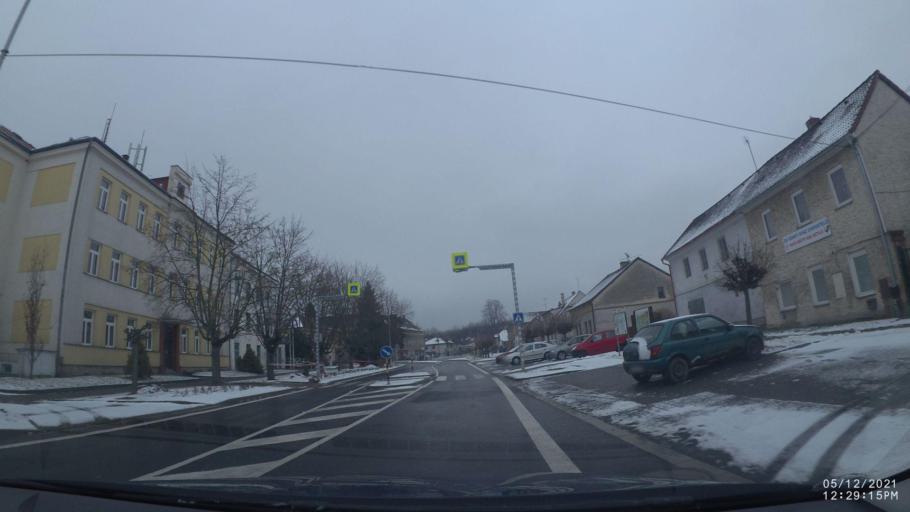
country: CZ
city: Nove Mesto nad Metuji
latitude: 50.3494
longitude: 16.1316
